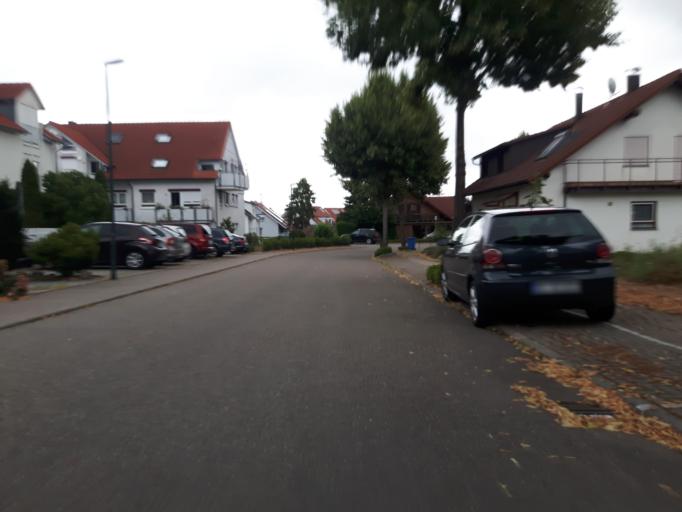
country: DE
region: Baden-Wuerttemberg
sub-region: Regierungsbezirk Stuttgart
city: Nordheim
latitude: 49.1052
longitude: 9.1093
